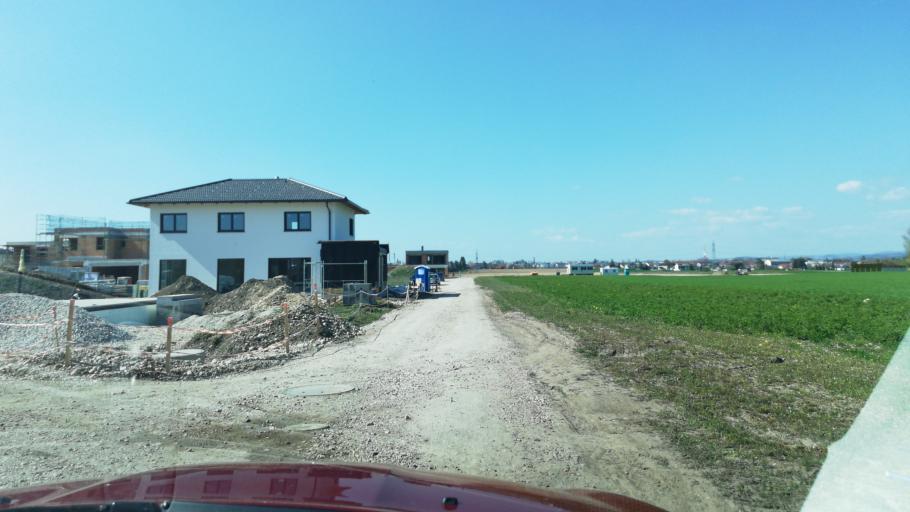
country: AT
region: Upper Austria
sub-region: Politischer Bezirk Linz-Land
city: Horsching
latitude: 48.2080
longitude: 14.1969
